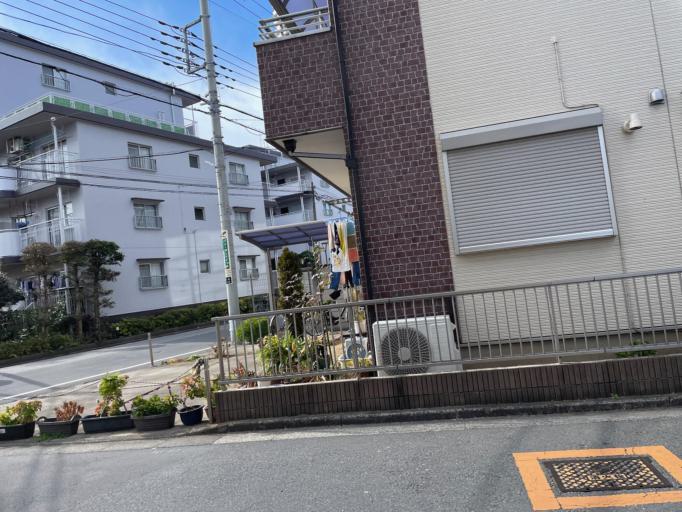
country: JP
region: Saitama
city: Kawaguchi
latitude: 35.8024
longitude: 139.7298
